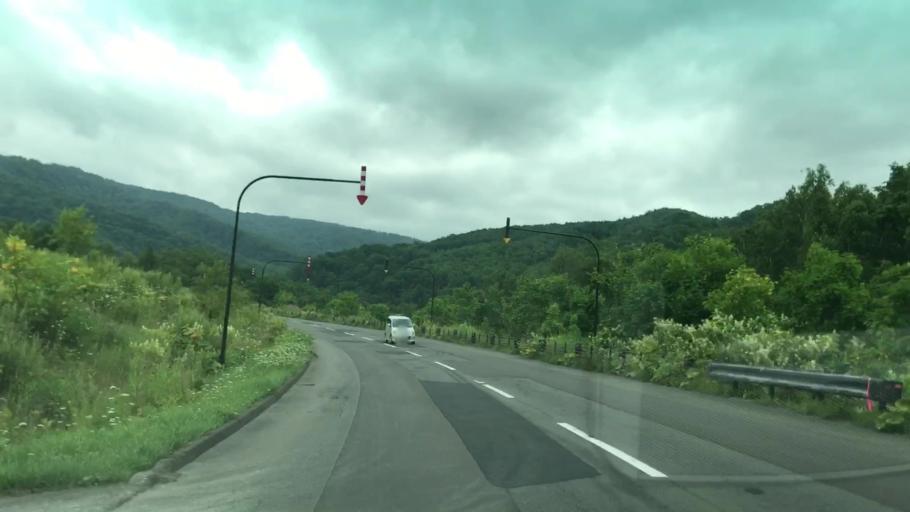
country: JP
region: Hokkaido
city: Yoichi
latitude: 43.0111
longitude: 140.8692
